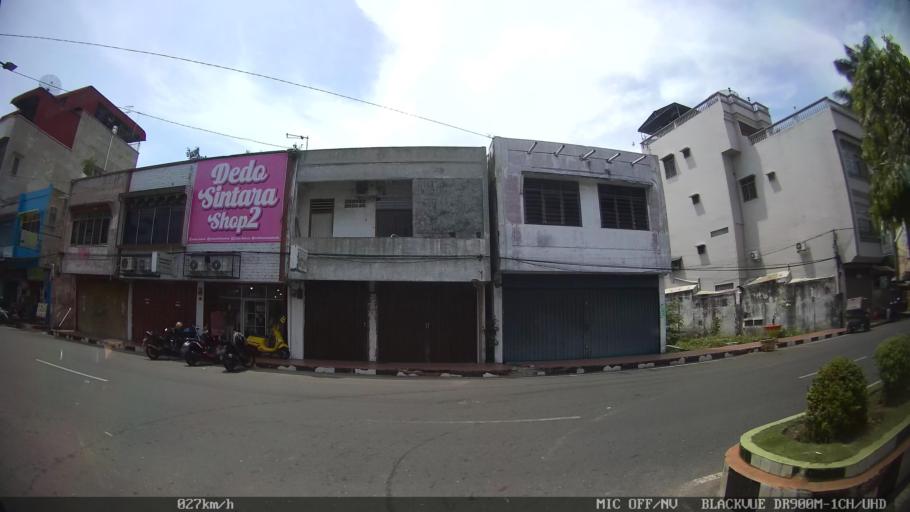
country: ID
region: North Sumatra
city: Binjai
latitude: 3.6038
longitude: 98.4839
